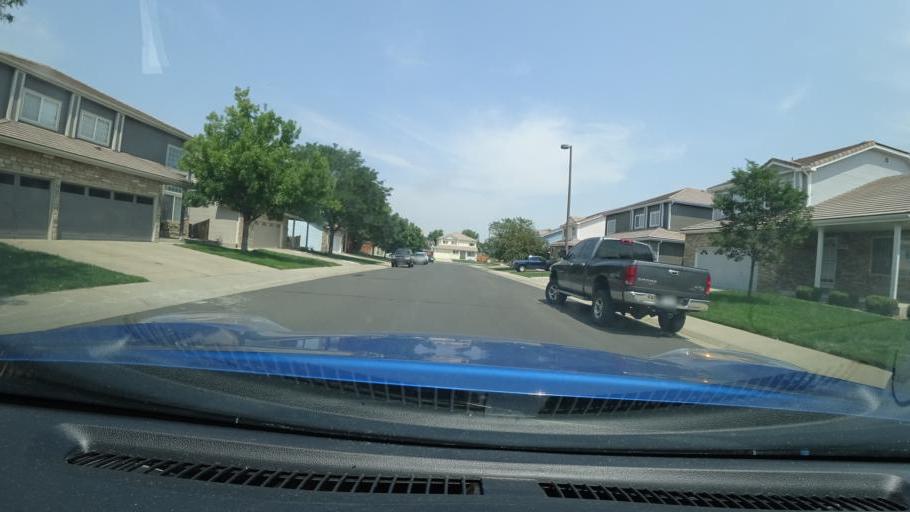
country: US
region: Colorado
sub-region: Adams County
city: Aurora
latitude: 39.7725
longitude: -104.7564
